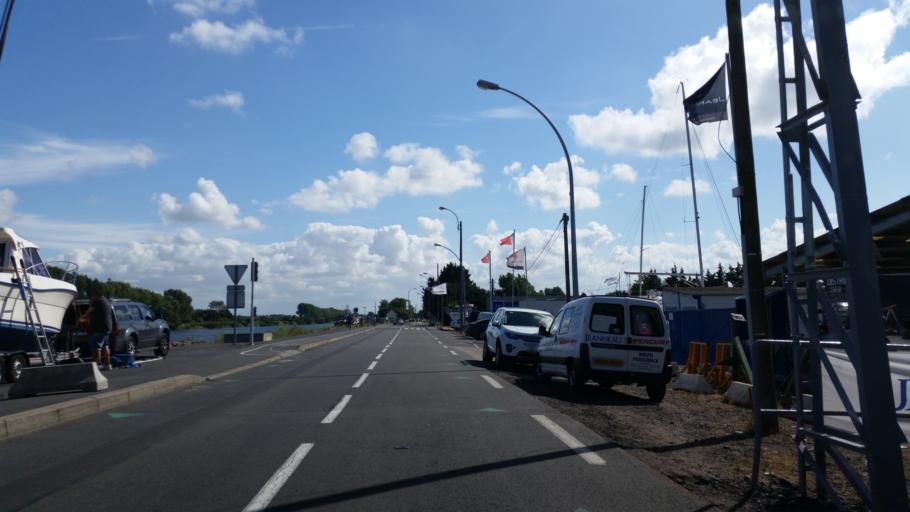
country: FR
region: Lower Normandy
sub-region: Departement du Calvados
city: Ouistreham
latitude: 49.2745
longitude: -0.2514
